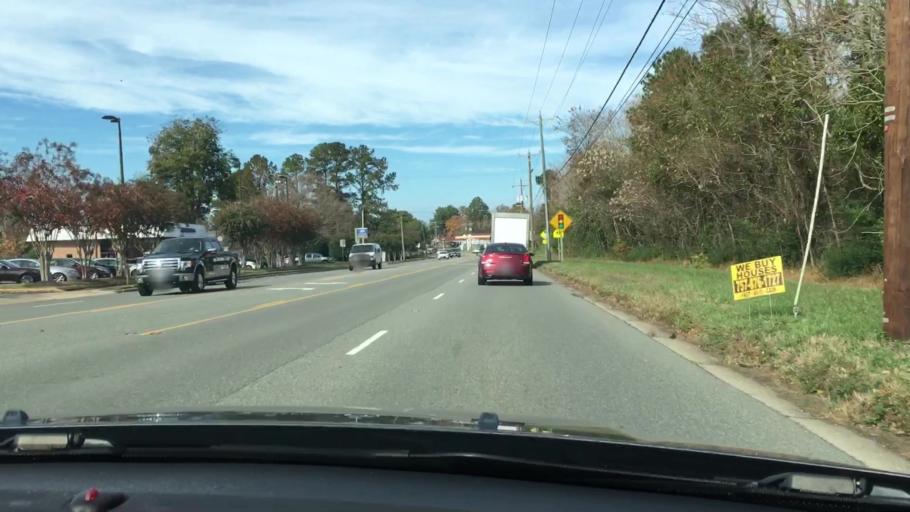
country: US
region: Virginia
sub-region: James City County
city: Williamsburg
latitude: 37.3623
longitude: -76.7661
